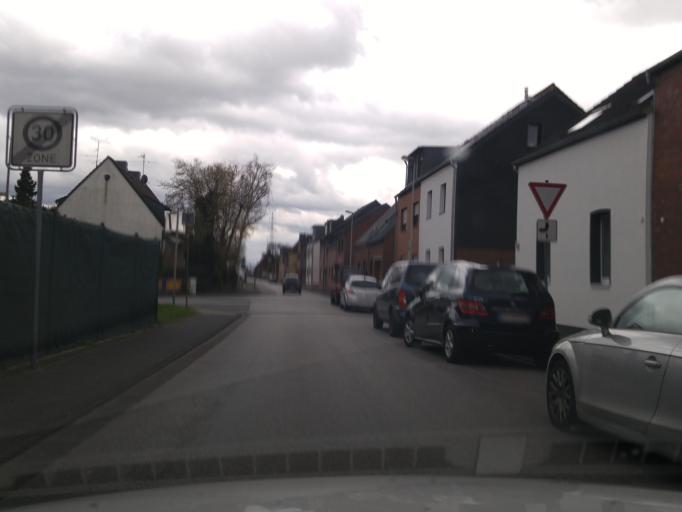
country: DE
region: North Rhine-Westphalia
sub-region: Regierungsbezirk Dusseldorf
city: Dormagen
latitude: 51.1379
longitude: 6.8206
